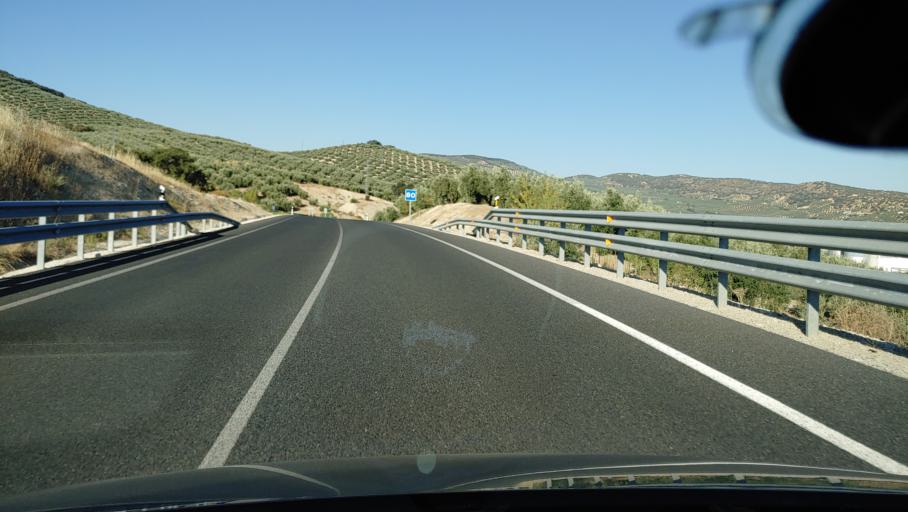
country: ES
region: Andalusia
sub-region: Provincia de Granada
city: Moclin
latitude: 37.3859
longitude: -3.8420
